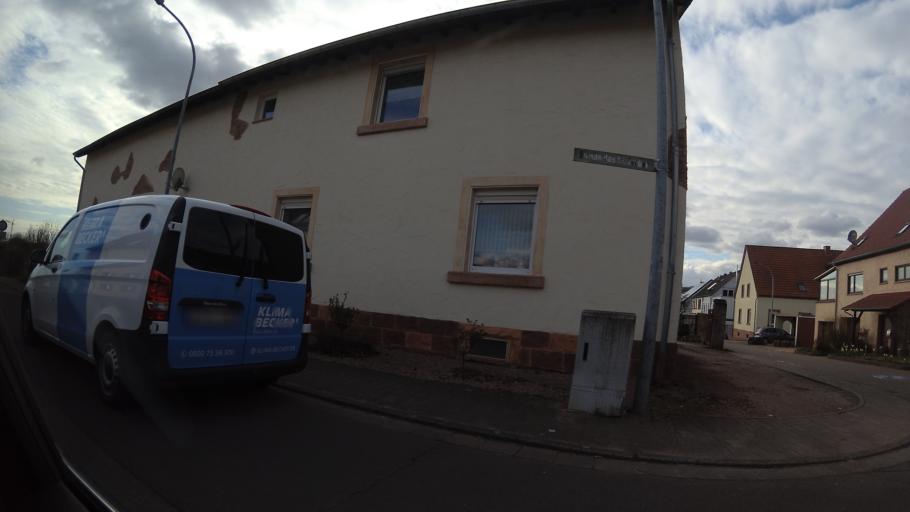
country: DE
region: Saarland
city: Blieskastel
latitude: 49.2374
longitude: 7.2734
